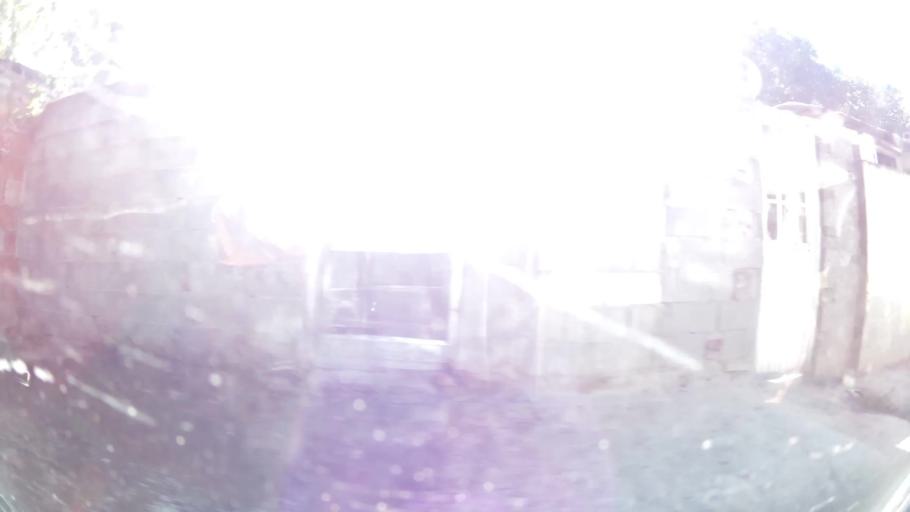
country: AR
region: Cordoba
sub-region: Departamento de Capital
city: Cordoba
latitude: -31.3764
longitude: -64.1893
